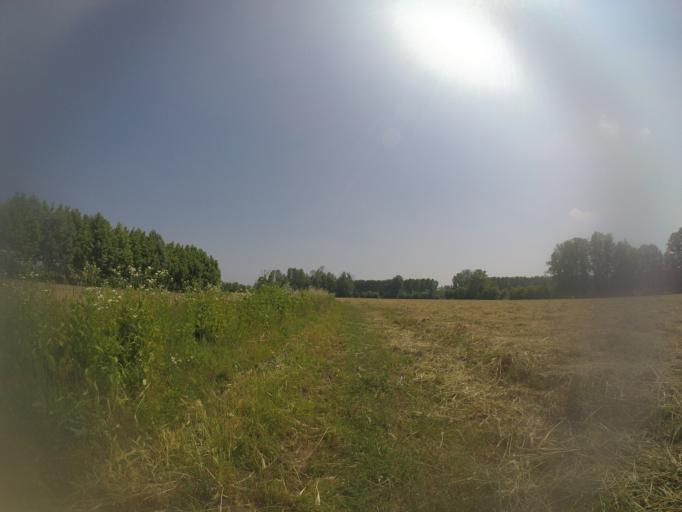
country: IT
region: Friuli Venezia Giulia
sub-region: Provincia di Udine
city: Bertiolo
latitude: 45.9328
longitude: 13.0349
